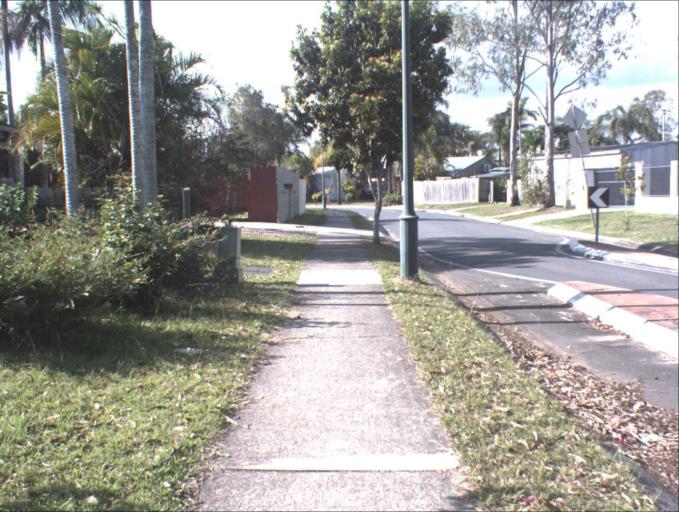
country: AU
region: Queensland
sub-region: Logan
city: Waterford West
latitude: -27.6894
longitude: 153.1263
